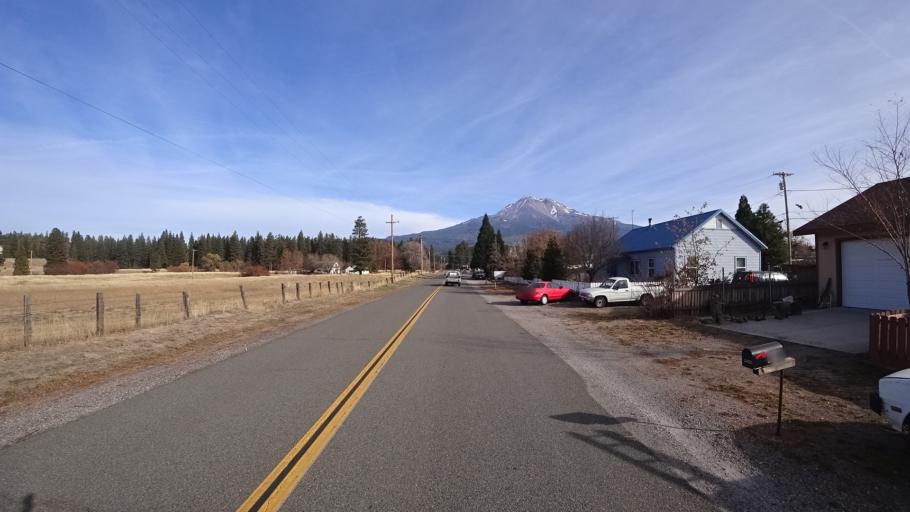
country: US
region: California
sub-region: Siskiyou County
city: Weed
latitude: 41.4392
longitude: -122.3809
